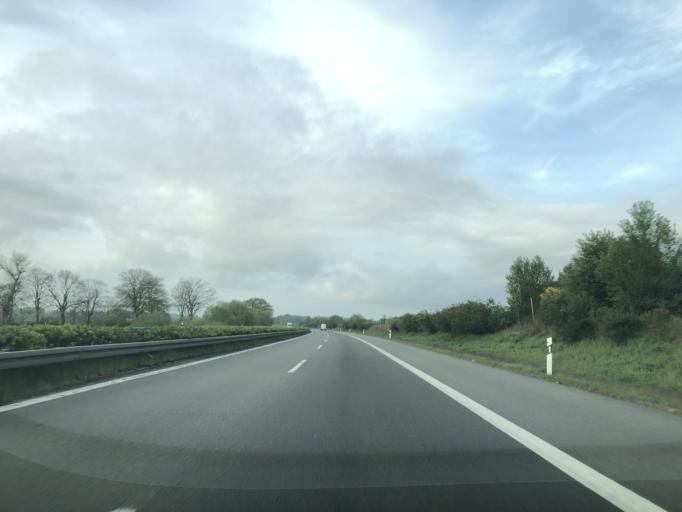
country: DE
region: Mecklenburg-Vorpommern
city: Bad Sulze
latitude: 54.0477
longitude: 12.6166
